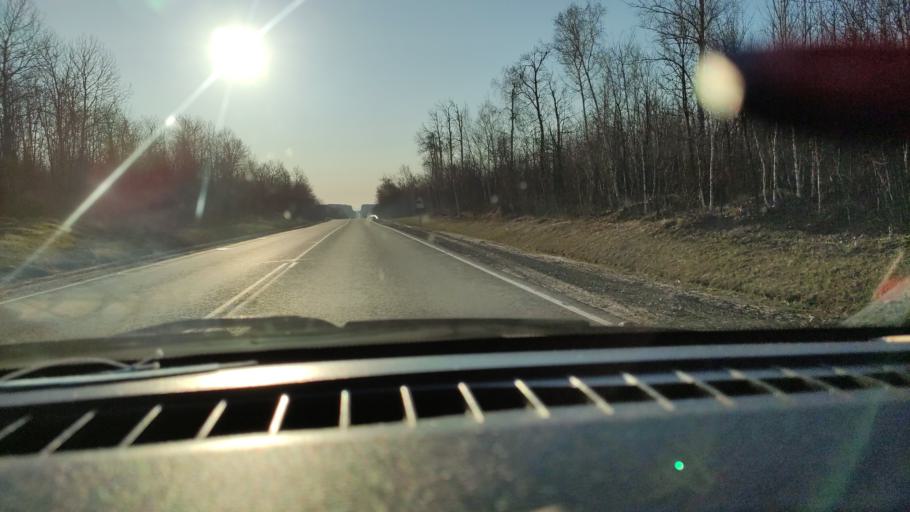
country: RU
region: Saratov
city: Vol'sk
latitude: 52.1099
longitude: 47.3639
